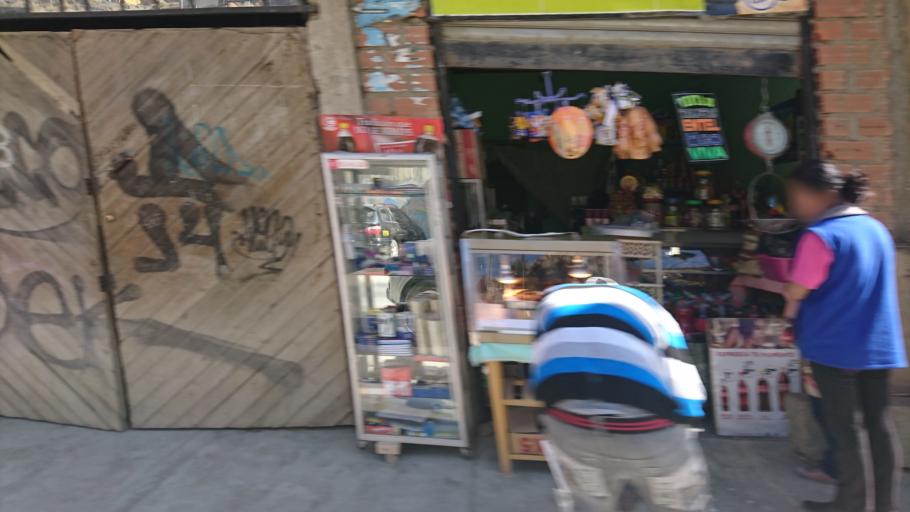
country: BO
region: La Paz
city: La Paz
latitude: -16.4810
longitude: -68.1148
